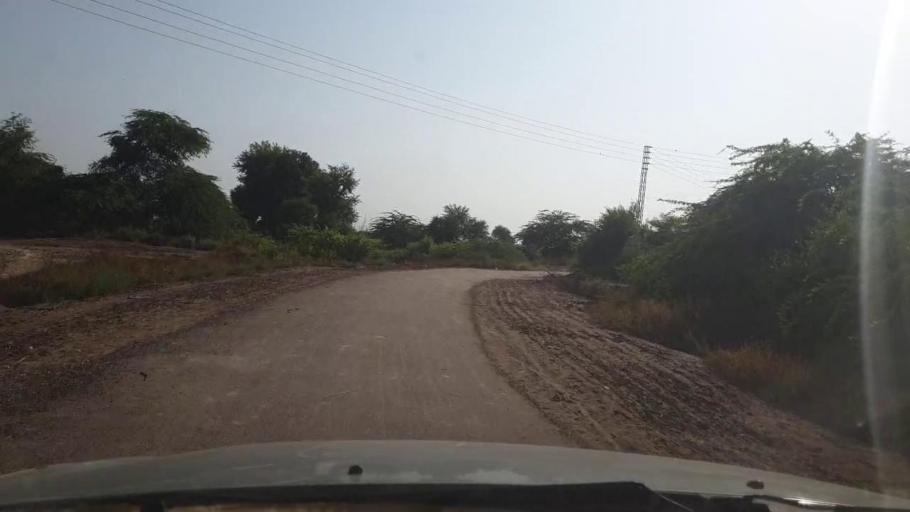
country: PK
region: Sindh
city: Tando Ghulam Ali
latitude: 25.2073
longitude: 68.9639
